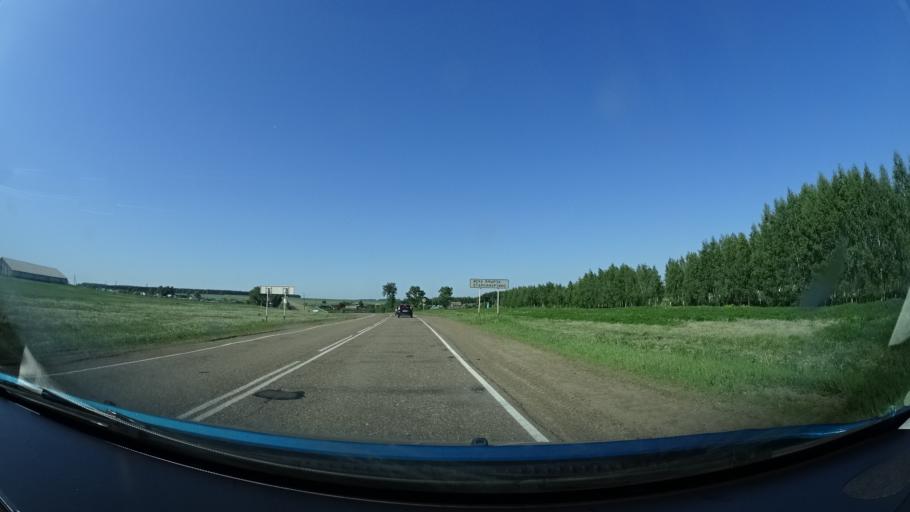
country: RU
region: Bashkortostan
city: Starobaltachevo
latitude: 55.9460
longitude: 55.8374
